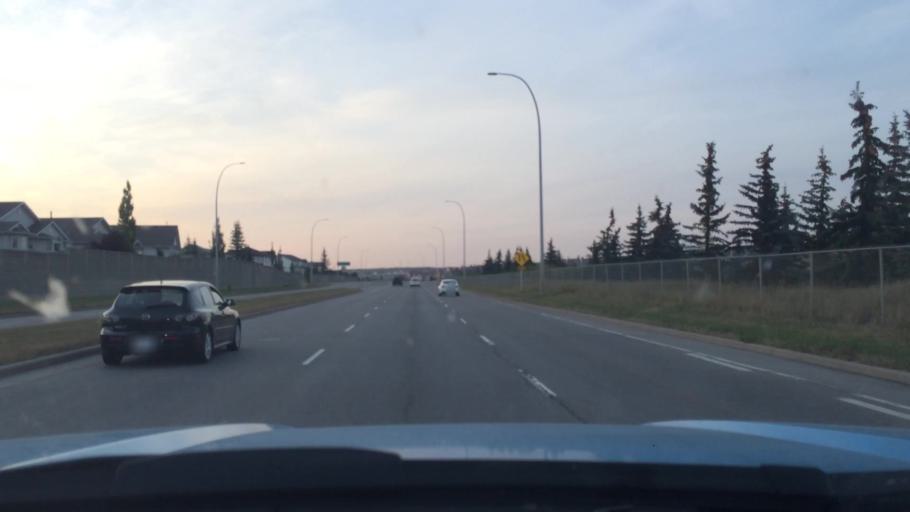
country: CA
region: Alberta
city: Calgary
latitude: 51.1471
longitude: -114.0956
